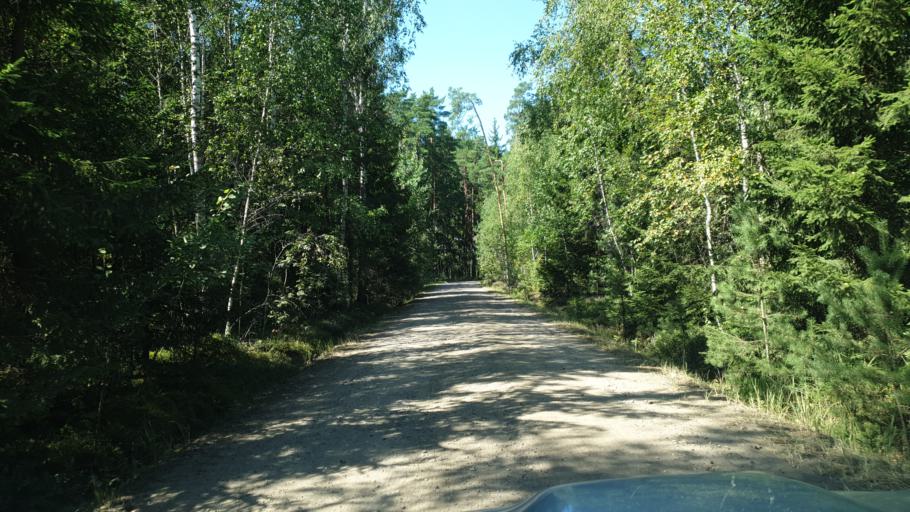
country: LT
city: Sirvintos
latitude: 54.9114
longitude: 24.9302
